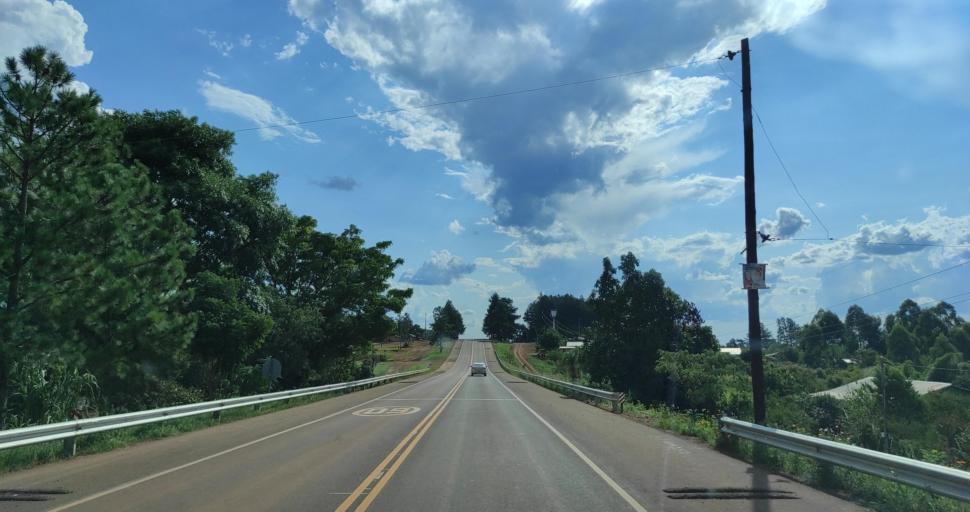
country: AR
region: Misiones
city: Bernardo de Irigoyen
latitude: -26.2963
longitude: -53.7925
